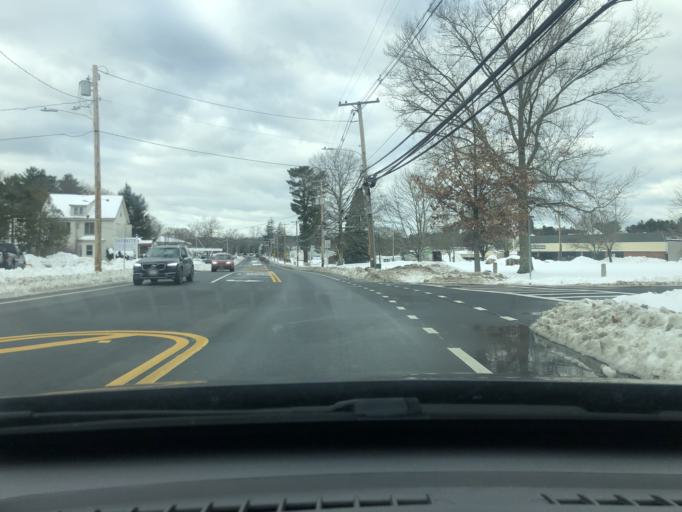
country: US
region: Massachusetts
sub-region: Middlesex County
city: Stow
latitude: 42.4326
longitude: -71.4843
